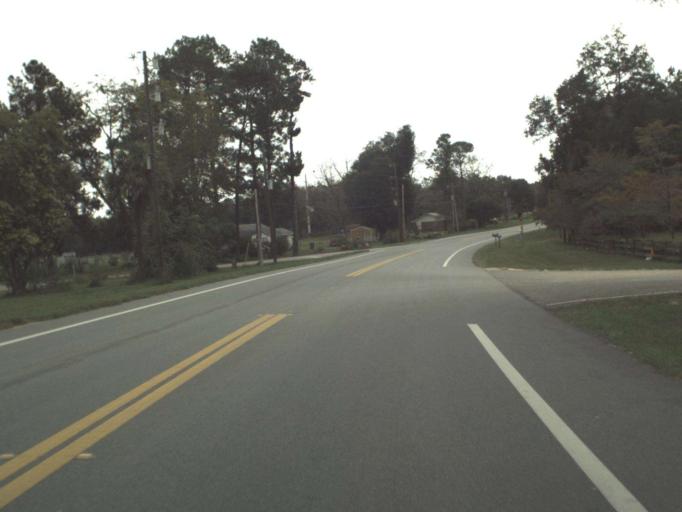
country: US
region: Florida
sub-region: Jackson County
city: Malone
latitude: 30.8529
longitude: -85.0778
